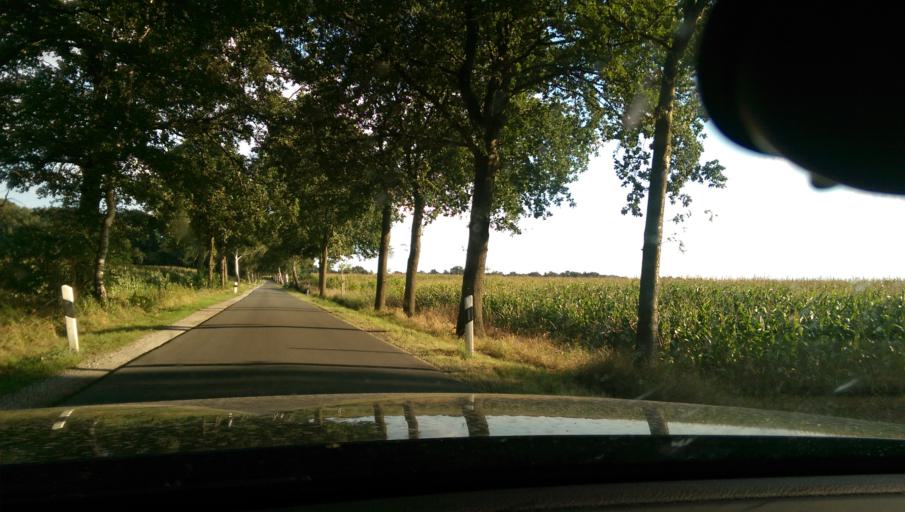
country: DE
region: Lower Saxony
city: Lindwedel
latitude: 52.5862
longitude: 9.6302
